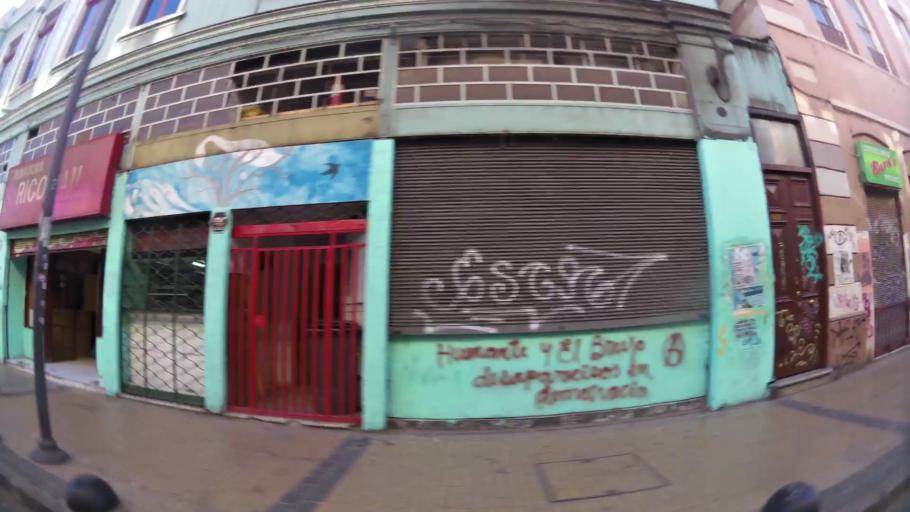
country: CL
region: Valparaiso
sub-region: Provincia de Valparaiso
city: Valparaiso
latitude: -33.0375
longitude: -71.6300
